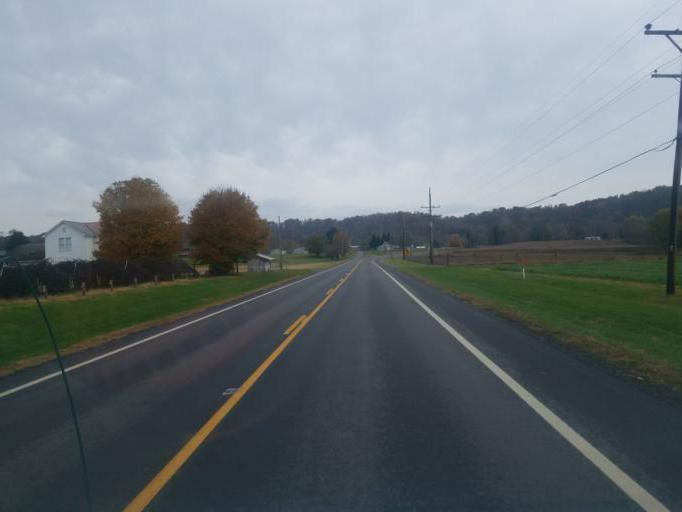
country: US
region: Ohio
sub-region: Washington County
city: Beverly
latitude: 39.5604
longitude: -81.5856
